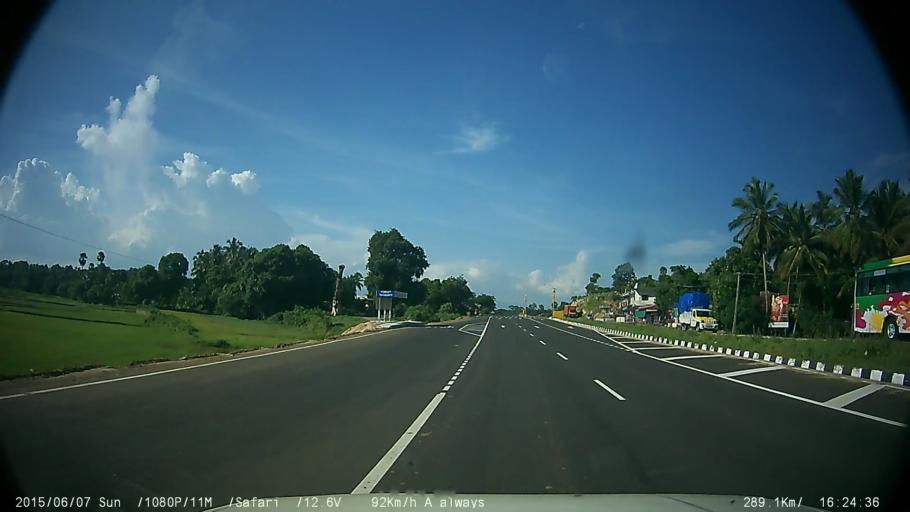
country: IN
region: Kerala
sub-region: Palakkad district
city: Palakkad
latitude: 10.6936
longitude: 76.5860
